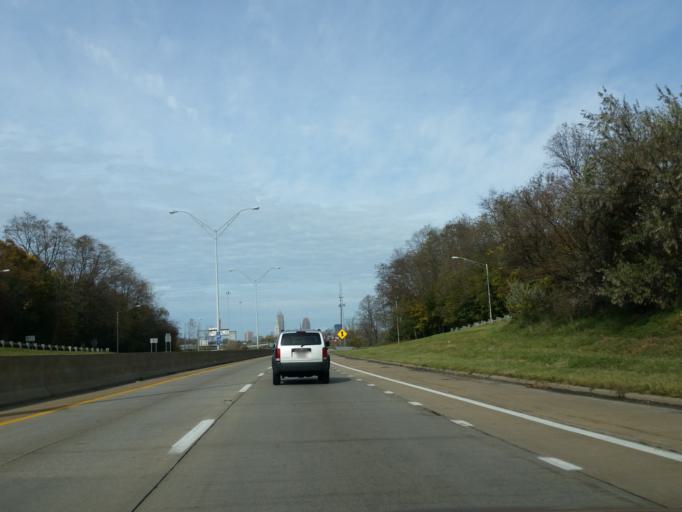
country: US
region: Ohio
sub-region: Cuyahoga County
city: Brooklyn Heights
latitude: 41.4525
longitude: -81.6906
